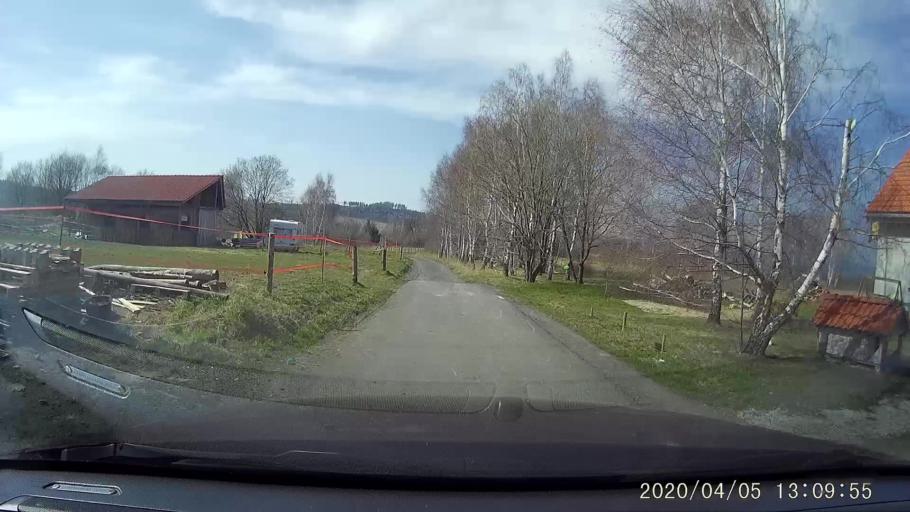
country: PL
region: Lower Silesian Voivodeship
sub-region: Powiat lubanski
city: Lesna
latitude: 50.9816
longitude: 15.2963
